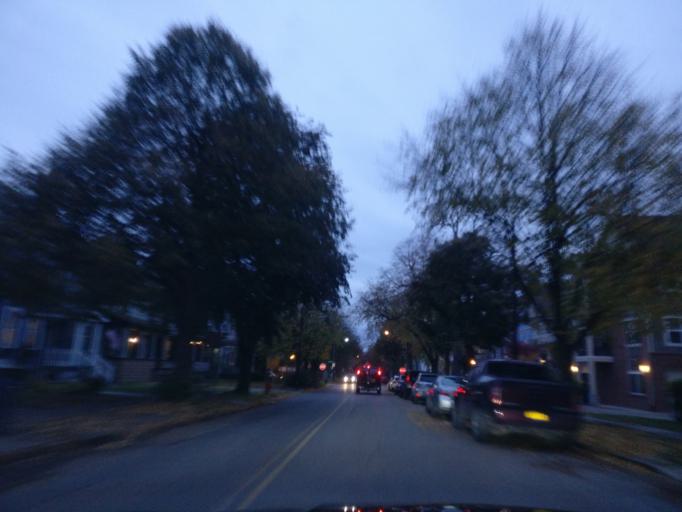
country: US
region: New York
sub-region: Erie County
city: Buffalo
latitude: 42.9113
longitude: -78.8776
